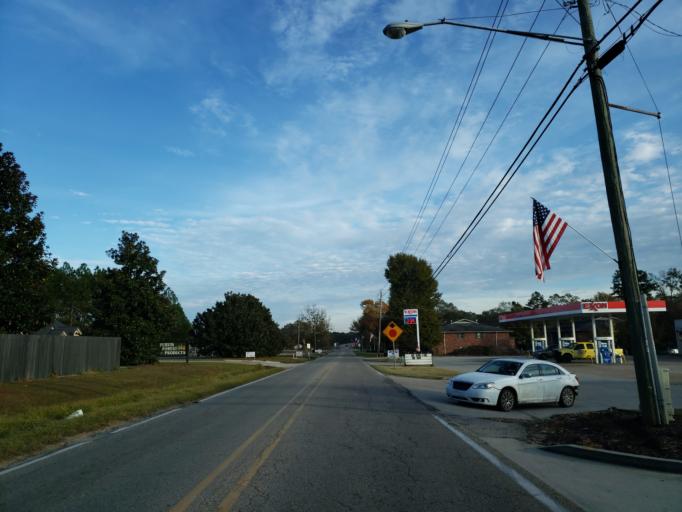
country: US
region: Mississippi
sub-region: Lamar County
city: Purvis
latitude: 31.1543
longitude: -89.4145
